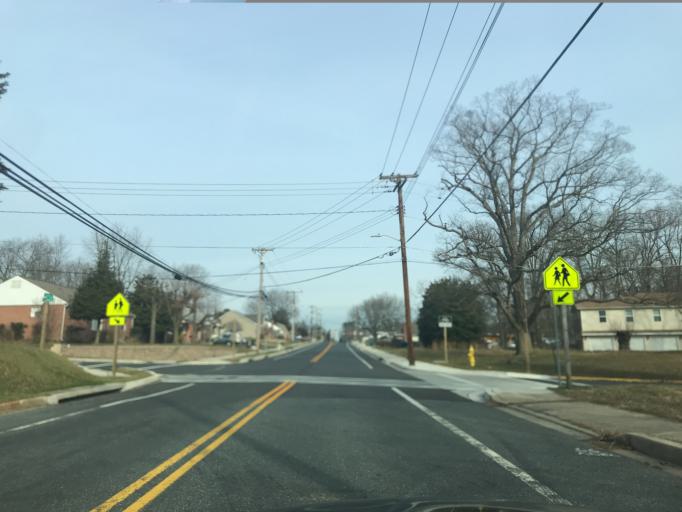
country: US
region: Maryland
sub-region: Harford County
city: Aberdeen
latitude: 39.5190
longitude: -76.1712
